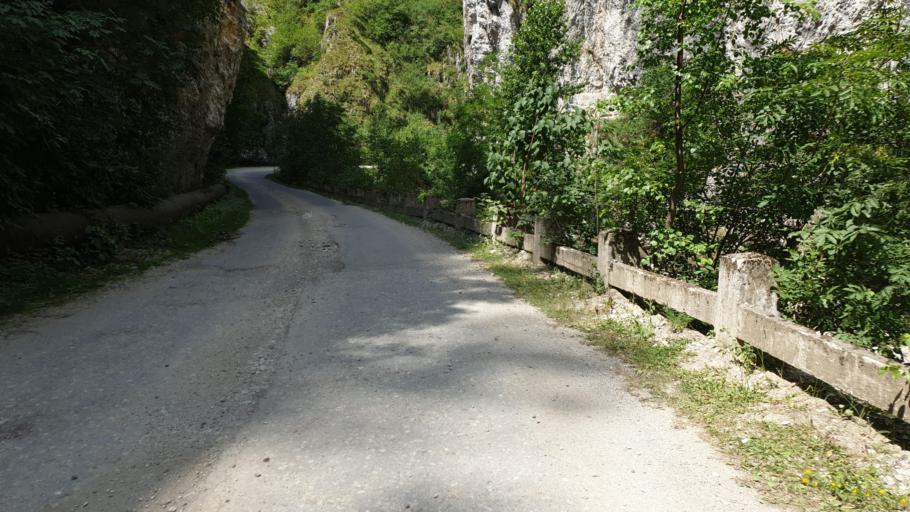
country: RO
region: Gorj
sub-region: Comuna Runcu
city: Runcu
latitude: 45.1365
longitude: 23.1413
